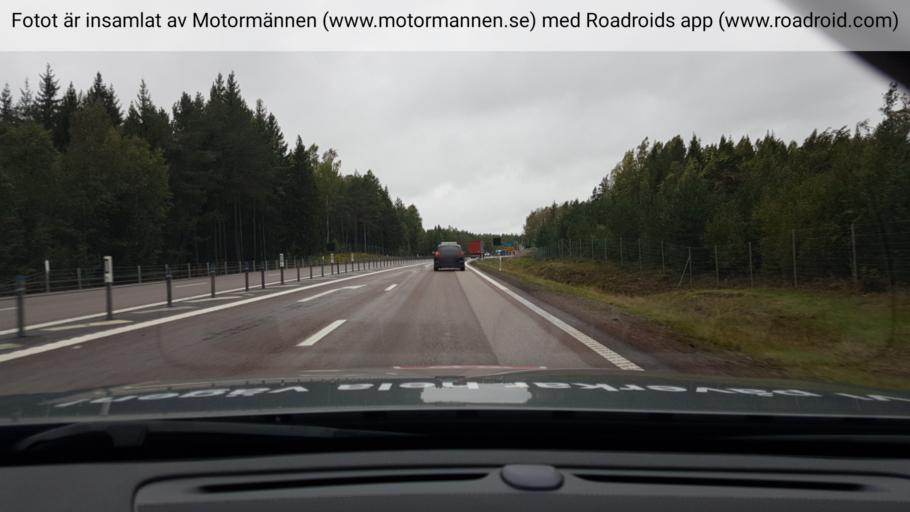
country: SE
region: Vaermland
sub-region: Kristinehamns Kommun
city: Kristinehamn
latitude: 59.3603
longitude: 14.0354
